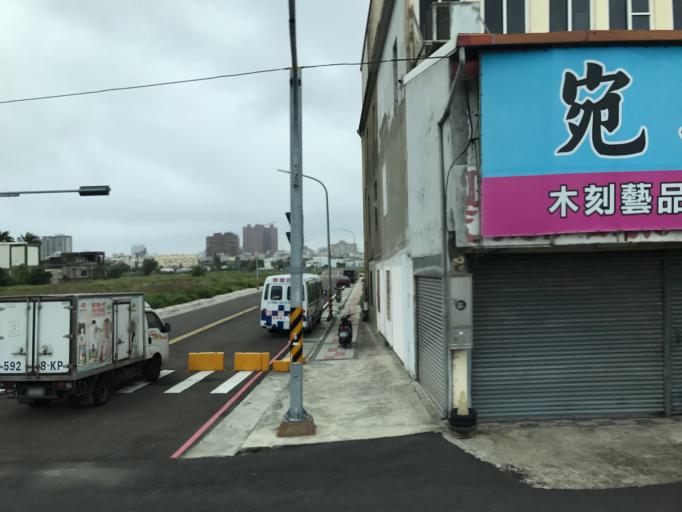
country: TW
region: Taiwan
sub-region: Hsinchu
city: Hsinchu
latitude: 24.8228
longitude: 120.9535
